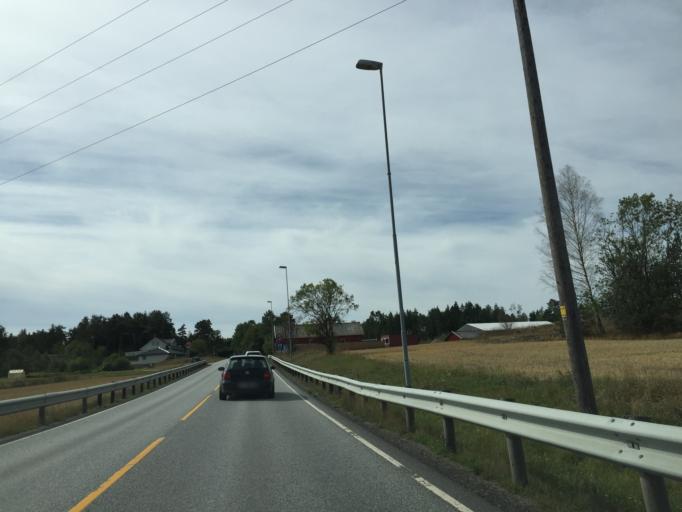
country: NO
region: Ostfold
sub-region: Fredrikstad
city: Fredrikstad
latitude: 59.2763
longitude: 10.9007
